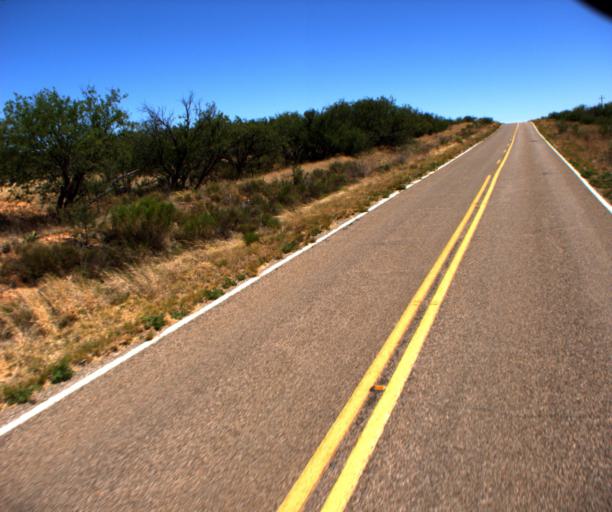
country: US
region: Arizona
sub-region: Santa Cruz County
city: Tubac
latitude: 31.5326
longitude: -111.5411
